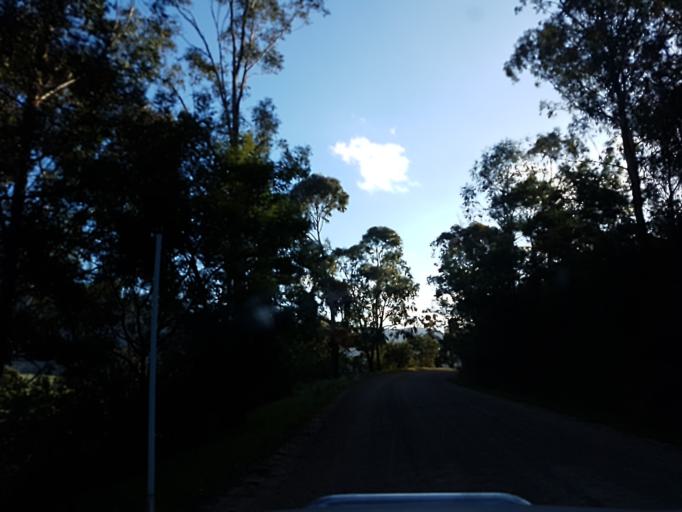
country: AU
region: Victoria
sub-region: East Gippsland
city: Bairnsdale
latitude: -37.4858
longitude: 147.1732
